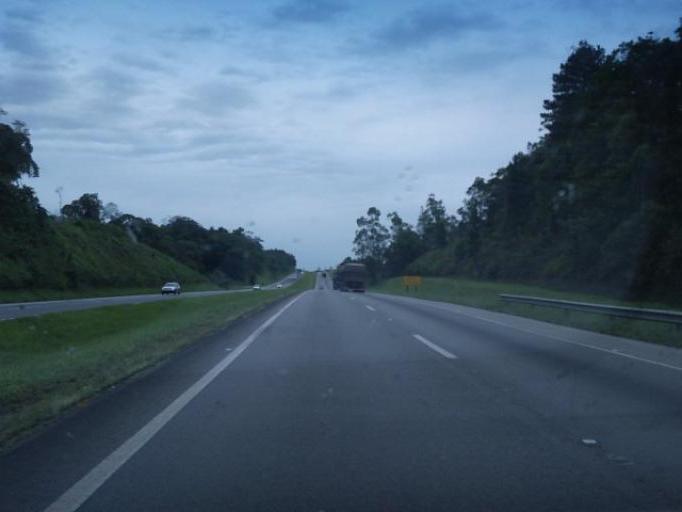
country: BR
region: Sao Paulo
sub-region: Registro
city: Registro
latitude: -24.4479
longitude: -47.8056
